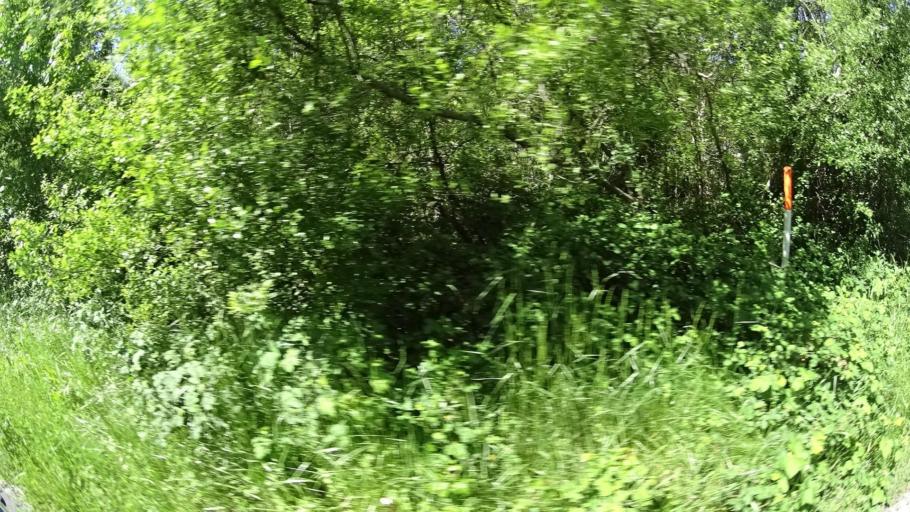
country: US
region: California
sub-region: Humboldt County
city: Rio Dell
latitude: 40.2345
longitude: -124.1170
